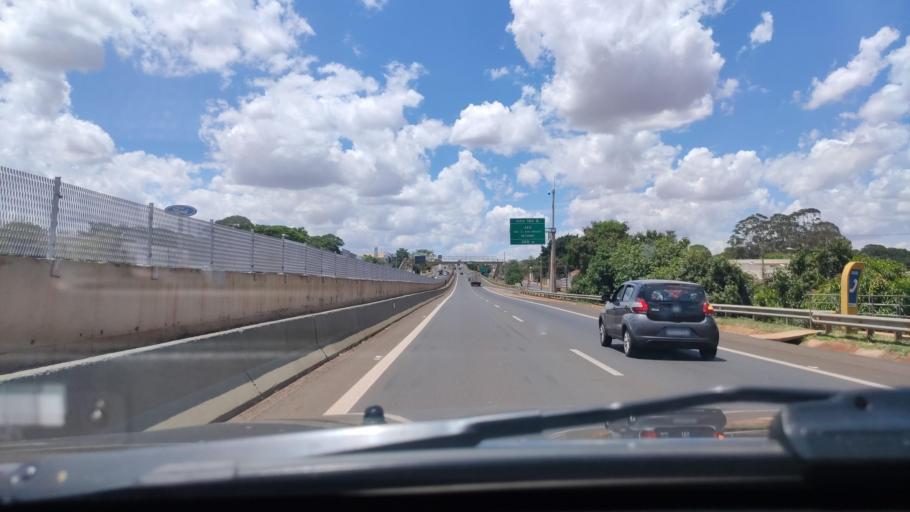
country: BR
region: Sao Paulo
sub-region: Jau
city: Jau
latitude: -22.2894
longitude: -48.5775
